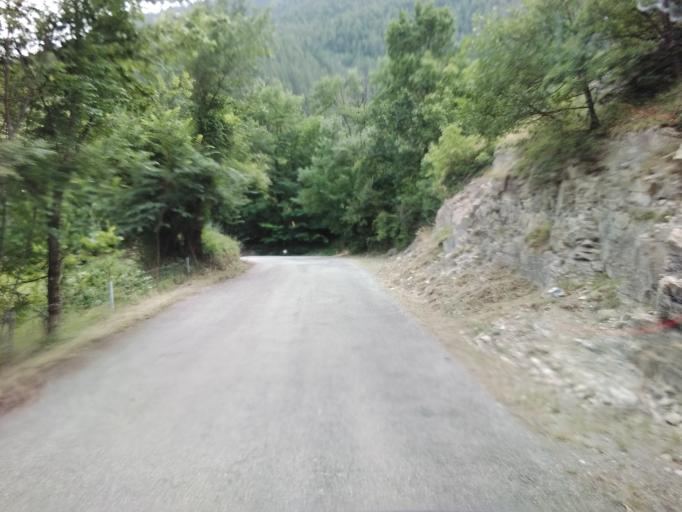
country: FR
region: Provence-Alpes-Cote d'Azur
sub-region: Departement des Alpes-de-Haute-Provence
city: Seyne-les-Alpes
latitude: 44.4340
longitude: 6.4281
